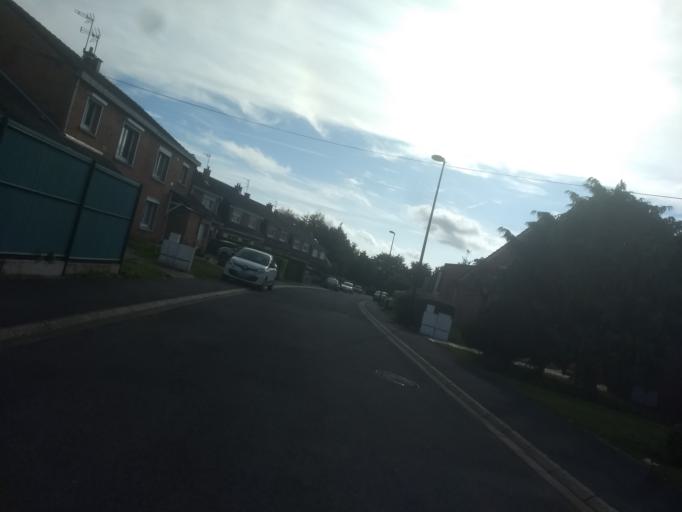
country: FR
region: Nord-Pas-de-Calais
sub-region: Departement du Pas-de-Calais
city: Dainville
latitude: 50.2850
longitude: 2.7319
